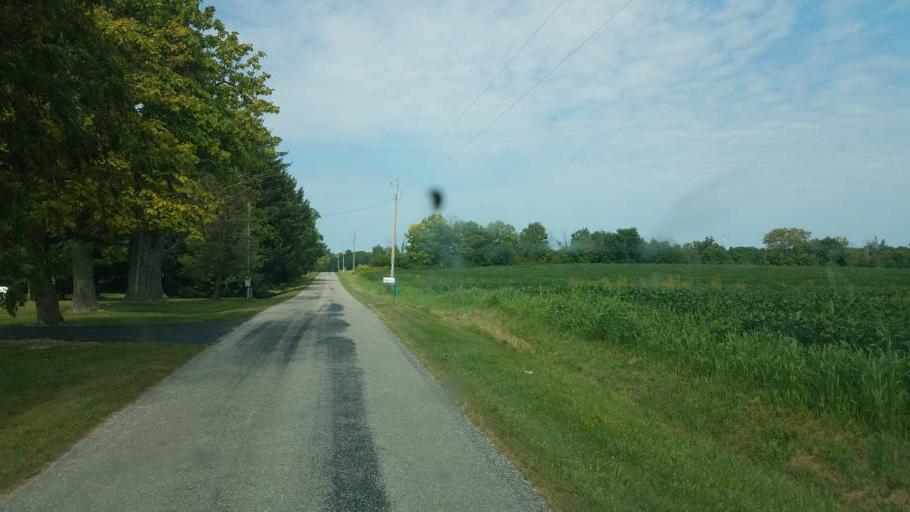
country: US
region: Ohio
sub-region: Delaware County
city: Ashley
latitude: 40.4454
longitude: -83.0337
